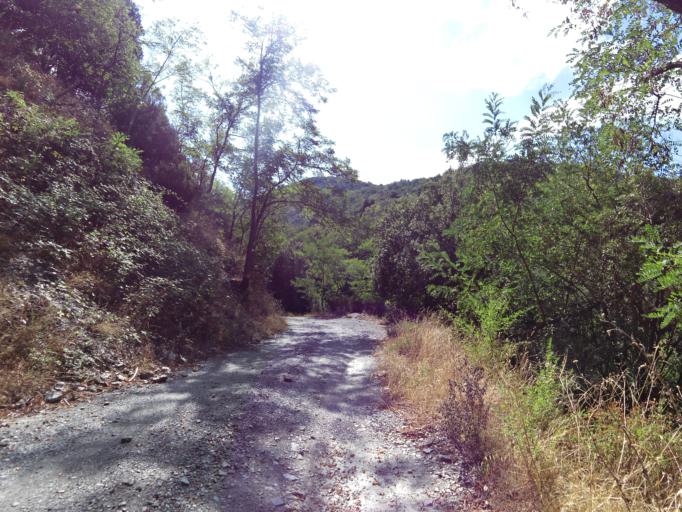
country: IT
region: Calabria
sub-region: Provincia di Reggio Calabria
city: Pazzano
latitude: 38.4687
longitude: 16.4312
